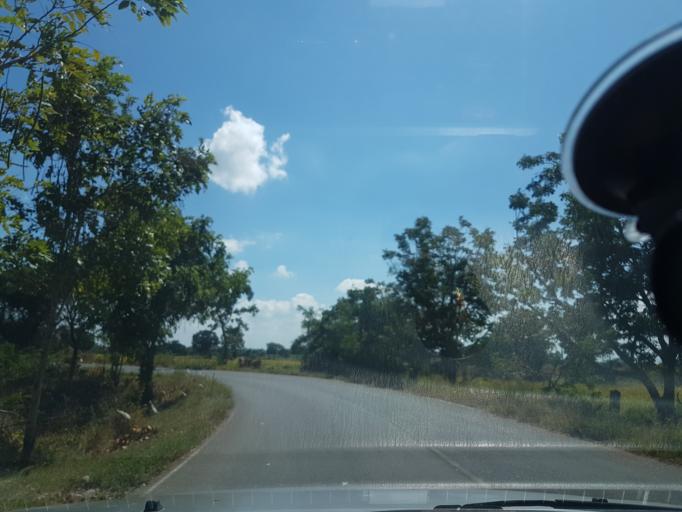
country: TH
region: Lop Buri
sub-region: Amphoe Tha Luang
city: Tha Luang
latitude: 14.9988
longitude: 101.0077
